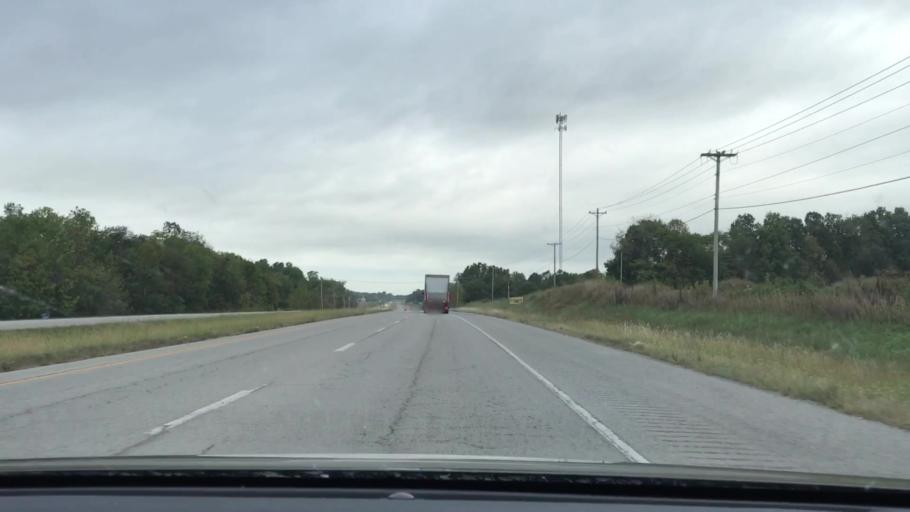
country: US
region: Kentucky
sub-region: Christian County
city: Hopkinsville
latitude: 36.8306
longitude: -87.5201
